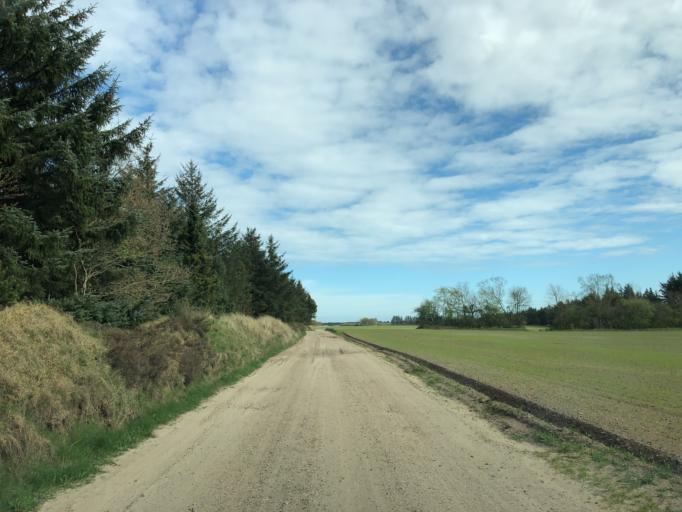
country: DK
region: Central Jutland
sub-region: Holstebro Kommune
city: Ulfborg
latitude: 56.2492
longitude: 8.3330
